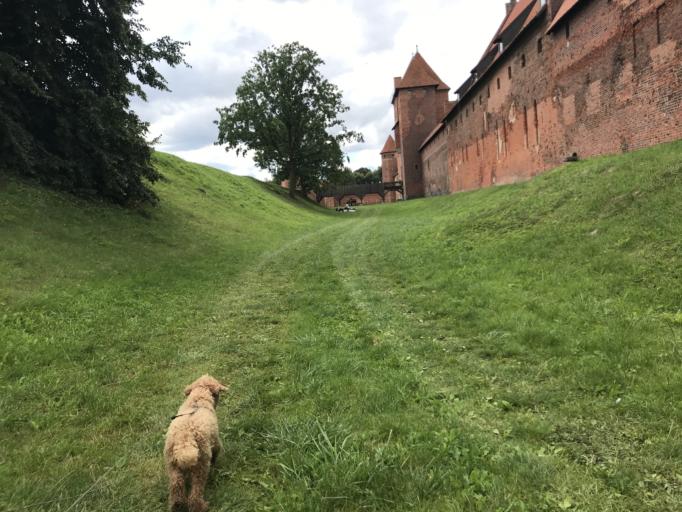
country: PL
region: Pomeranian Voivodeship
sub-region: Powiat malborski
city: Malbork
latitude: 54.0412
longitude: 19.0320
